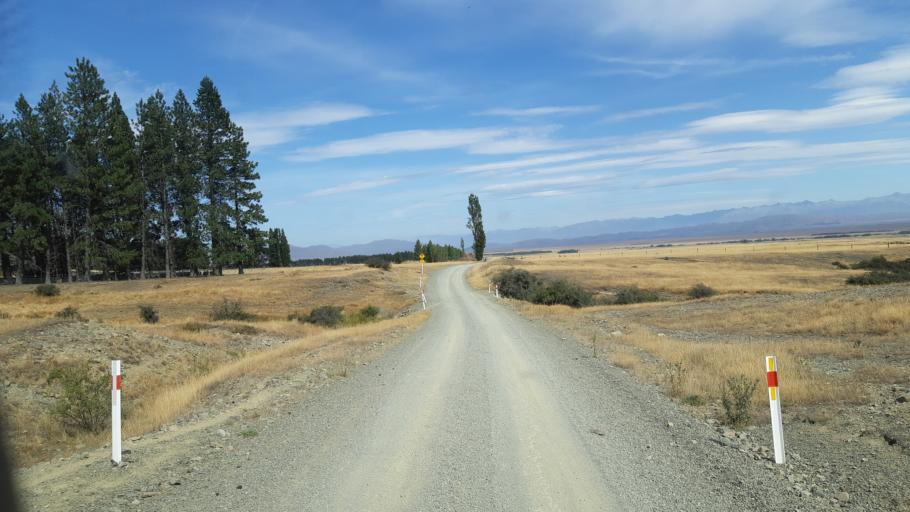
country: NZ
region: Canterbury
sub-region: Timaru District
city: Pleasant Point
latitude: -44.1936
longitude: 170.5689
